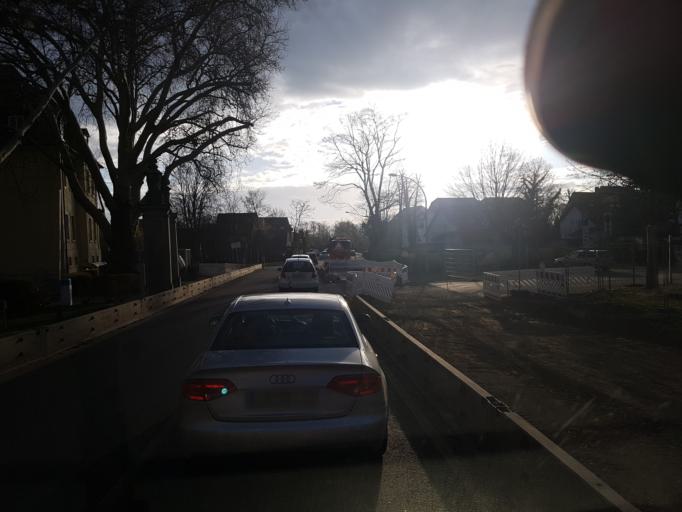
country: DE
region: Brandenburg
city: Luebben
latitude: 51.9407
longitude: 13.8997
